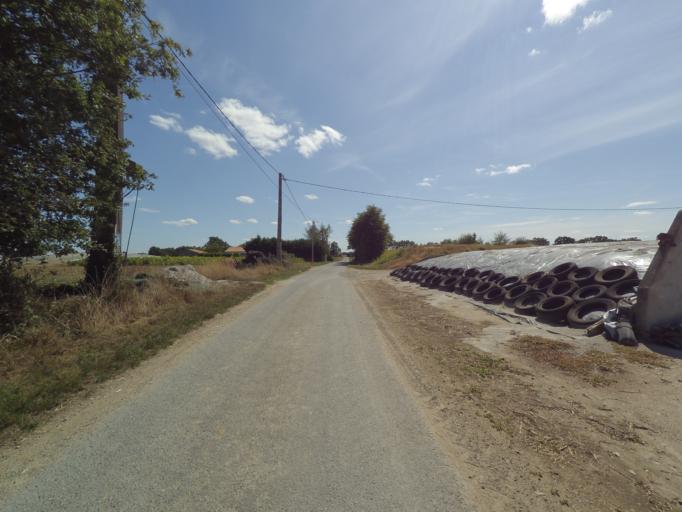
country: FR
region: Pays de la Loire
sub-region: Departement de la Loire-Atlantique
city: Vieillevigne
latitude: 46.9745
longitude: -1.3910
